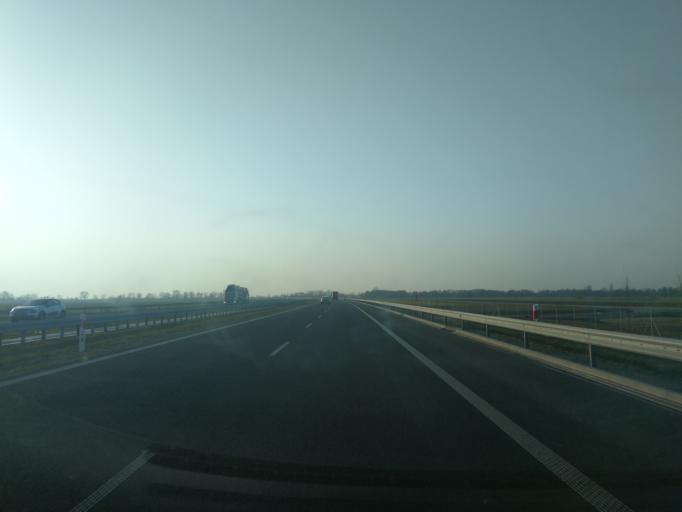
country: PL
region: Pomeranian Voivodeship
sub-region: Powiat malborski
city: Stare Pole
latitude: 54.1700
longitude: 19.2245
